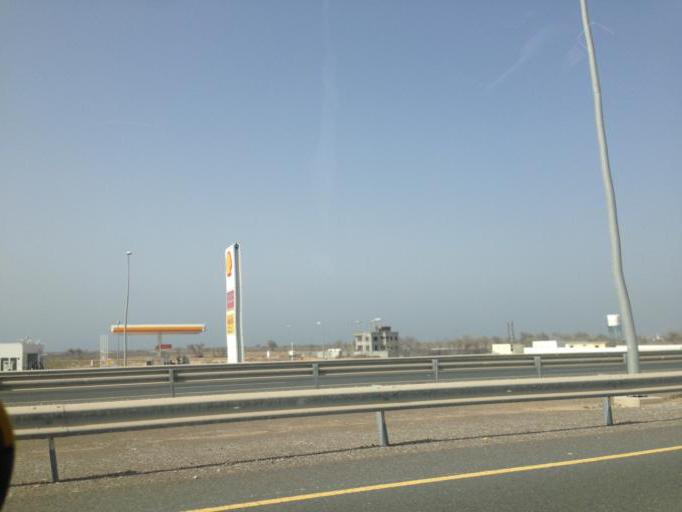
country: OM
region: Al Batinah
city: Barka'
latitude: 23.6994
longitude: 58.0076
